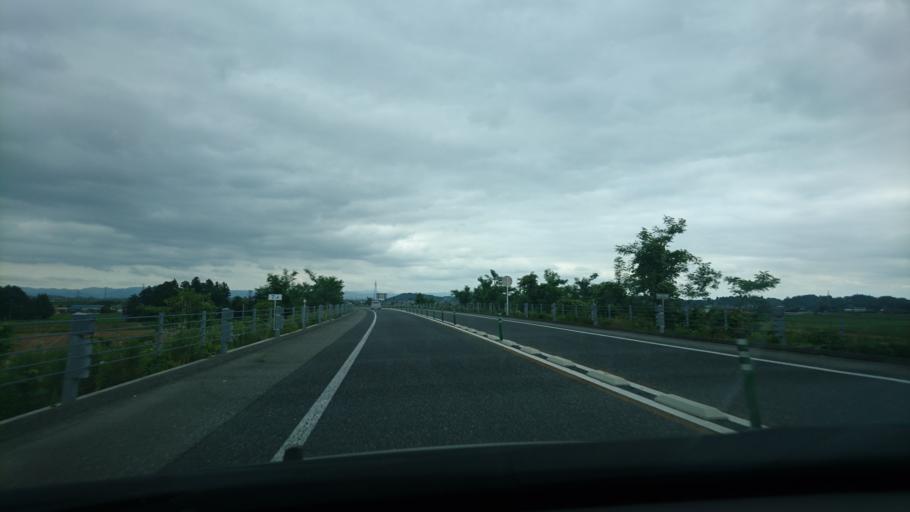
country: JP
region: Miyagi
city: Wakuya
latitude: 38.7290
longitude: 141.1373
